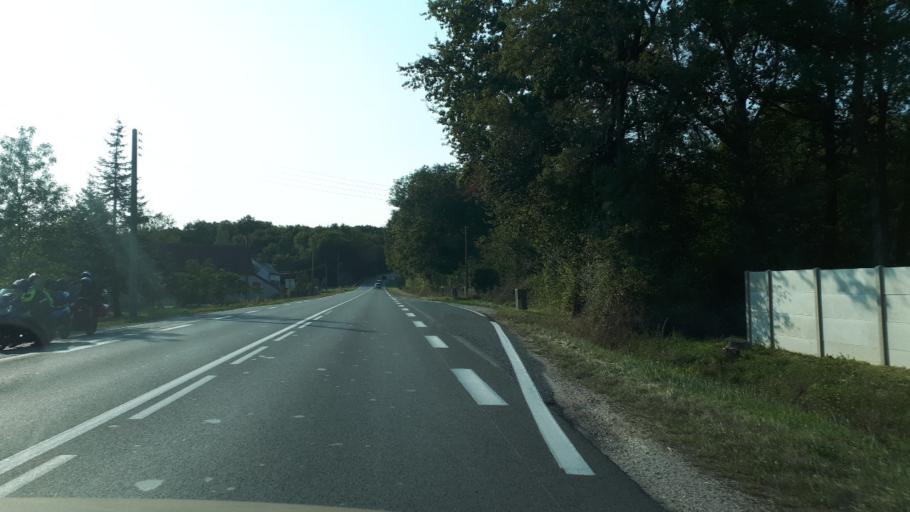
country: FR
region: Centre
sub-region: Departement du Cher
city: Vignoux-sur-Barangeon
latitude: 47.2045
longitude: 2.1654
